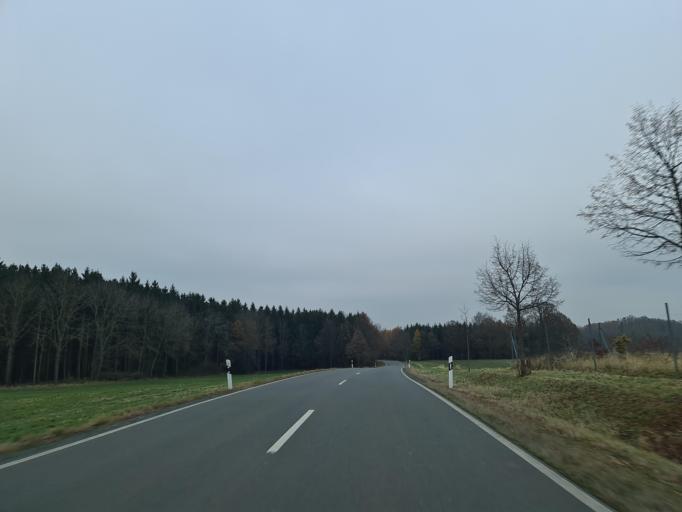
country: DE
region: Saxony
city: Syrau
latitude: 50.5108
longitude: 12.0754
